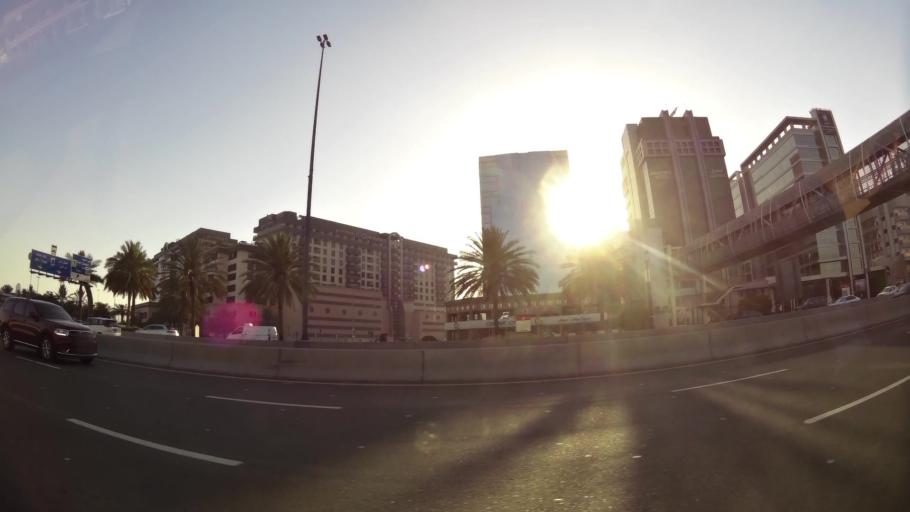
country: AE
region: Ash Shariqah
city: Sharjah
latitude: 25.2520
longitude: 55.3363
